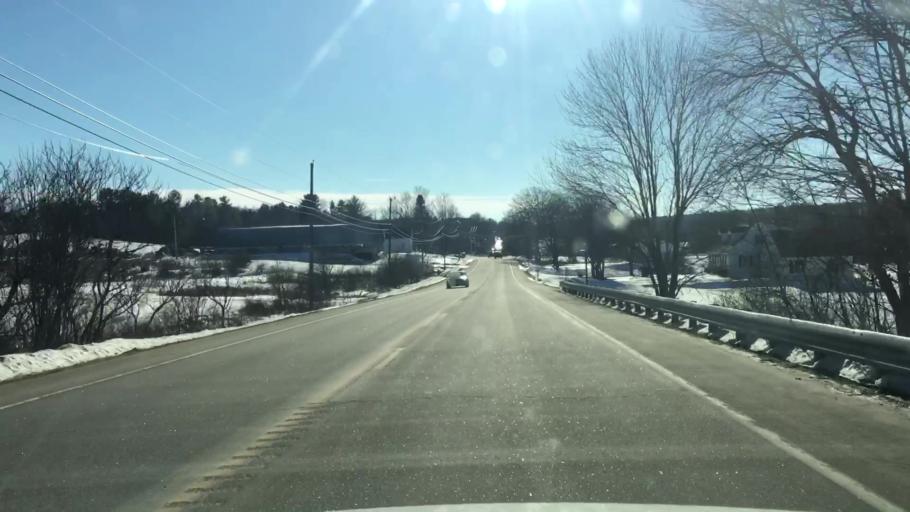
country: US
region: Maine
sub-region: Cumberland County
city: North Windham
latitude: 43.8124
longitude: -70.4008
